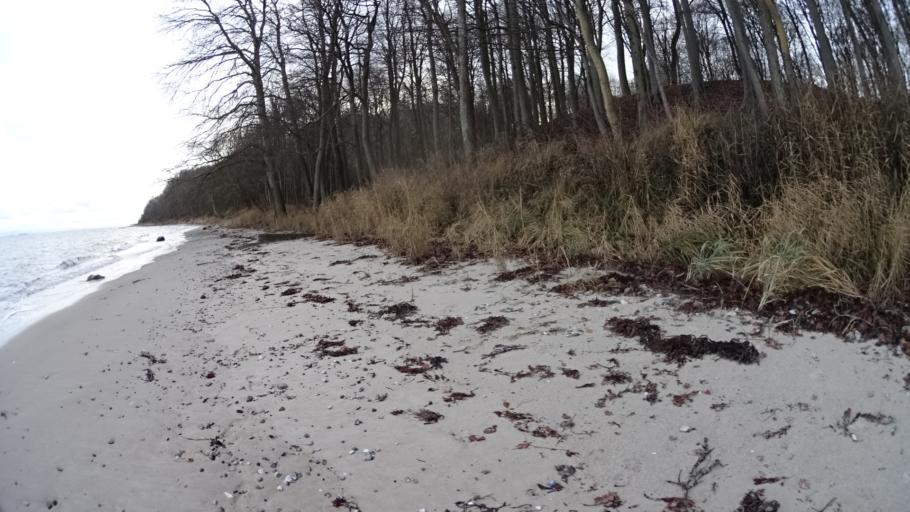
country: DK
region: Central Jutland
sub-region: Arhus Kommune
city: Beder
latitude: 56.0710
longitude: 10.2559
